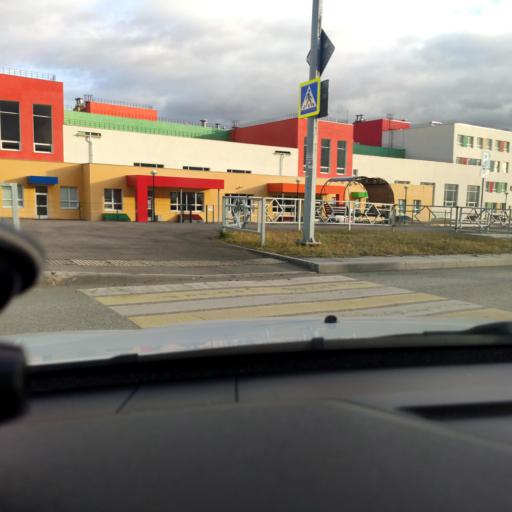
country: RU
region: Samara
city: Petra-Dubrava
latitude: 53.2984
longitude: 50.3292
